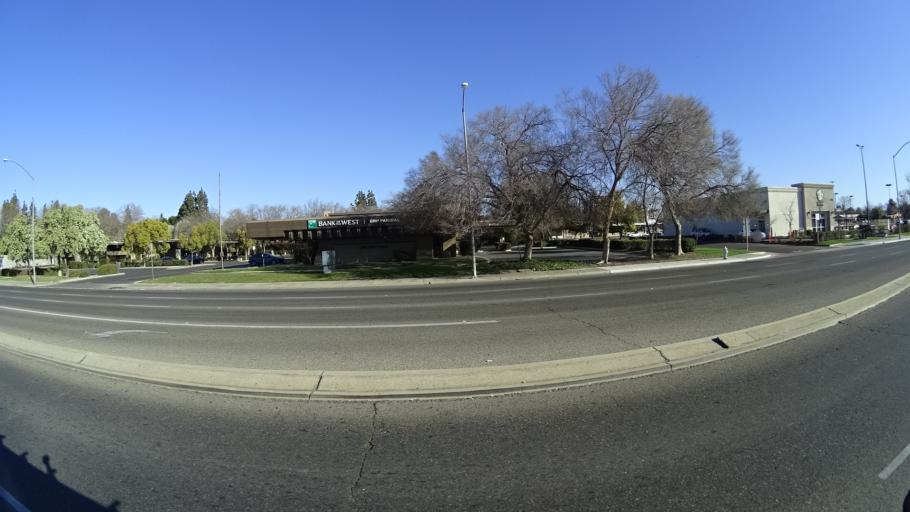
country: US
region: California
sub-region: Fresno County
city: Fresno
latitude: 36.8082
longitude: -119.8288
